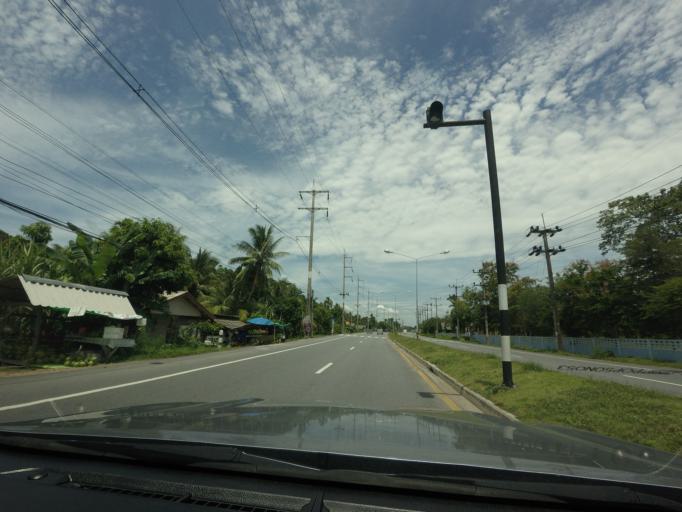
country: TH
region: Songkhla
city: Krasae Sin
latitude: 7.5761
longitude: 100.4090
